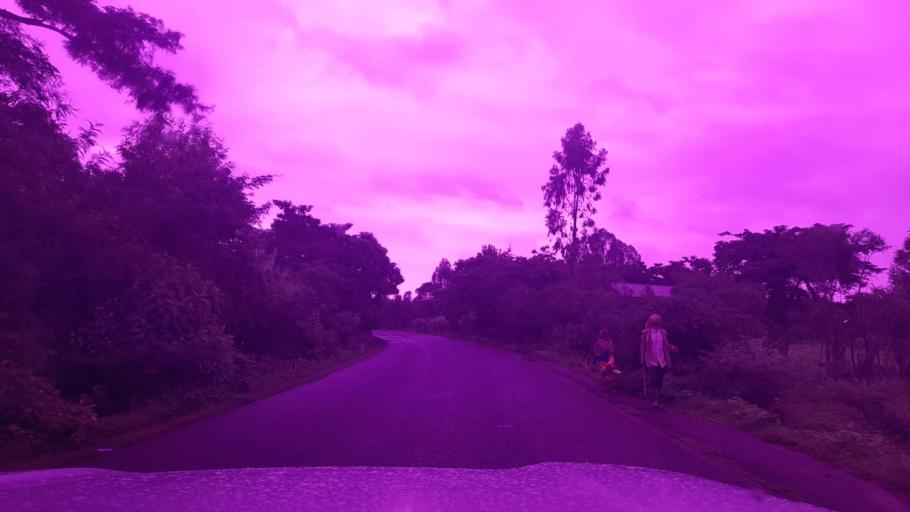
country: ET
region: Oromiya
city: Jima
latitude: 7.7122
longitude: 37.2521
